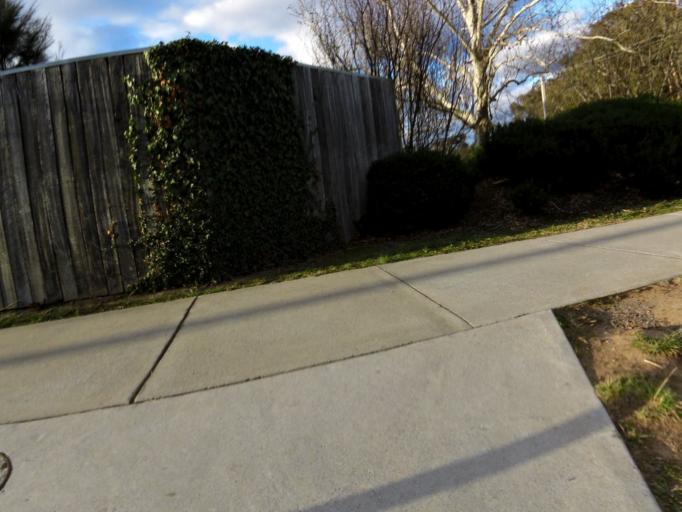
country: AU
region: Australian Capital Territory
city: Acton
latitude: -35.2722
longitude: 149.1173
